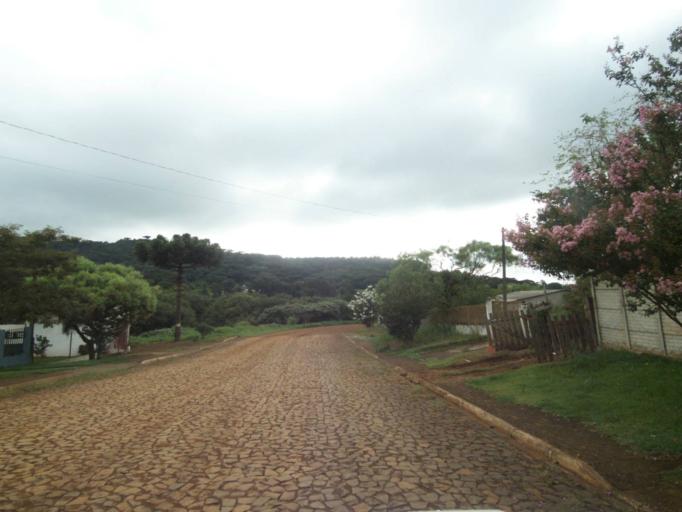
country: BR
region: Parana
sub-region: Pitanga
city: Pitanga
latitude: -24.9358
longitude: -51.8708
